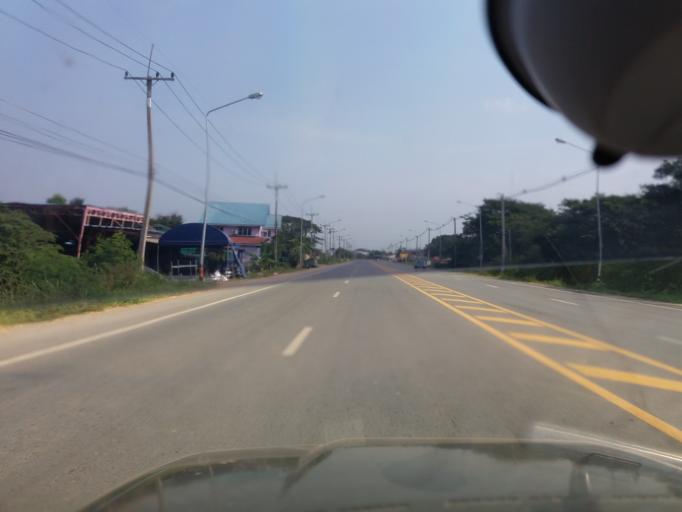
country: TH
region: Sing Buri
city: Sing Buri
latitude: 14.8859
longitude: 100.3744
